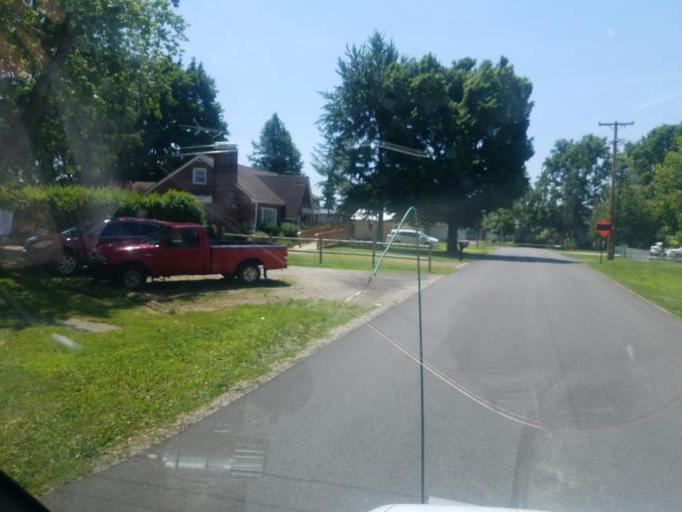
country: US
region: Ohio
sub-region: Logan County
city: West Liberty
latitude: 40.2531
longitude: -83.7507
